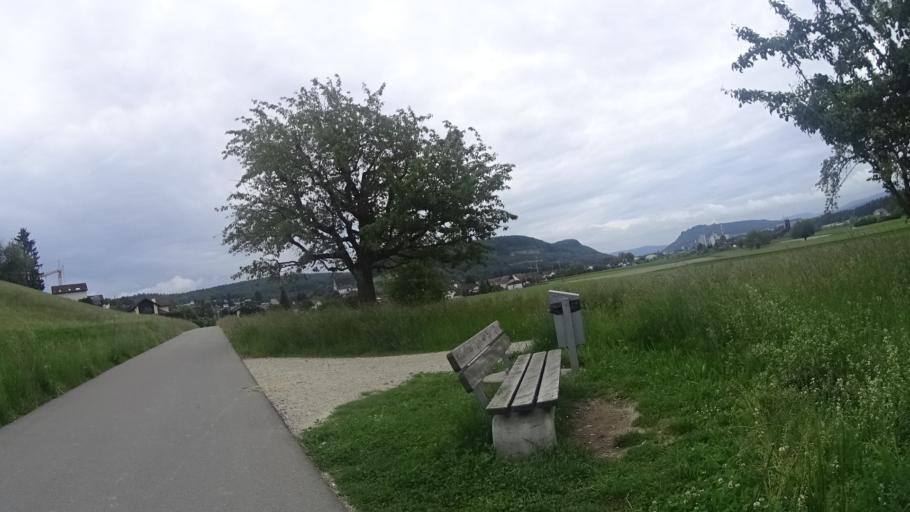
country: CH
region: Aargau
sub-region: Bezirk Baden
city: Wurenlingen
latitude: 47.5411
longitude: 8.2559
